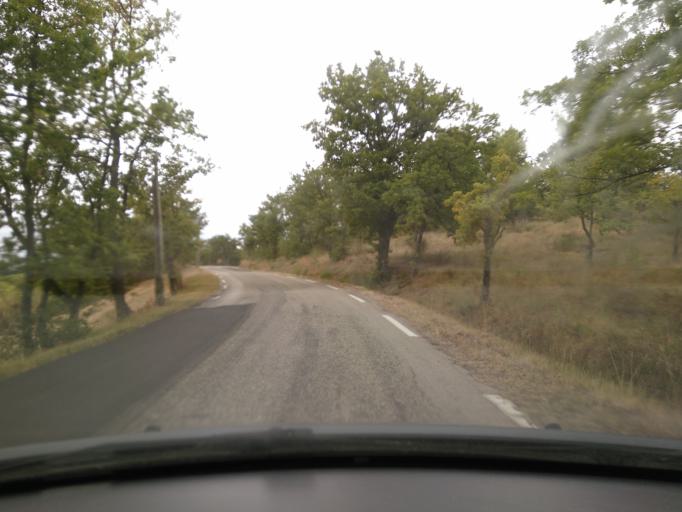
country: FR
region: Provence-Alpes-Cote d'Azur
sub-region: Departement du Vaucluse
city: Valreas
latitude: 44.3641
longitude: 5.0148
